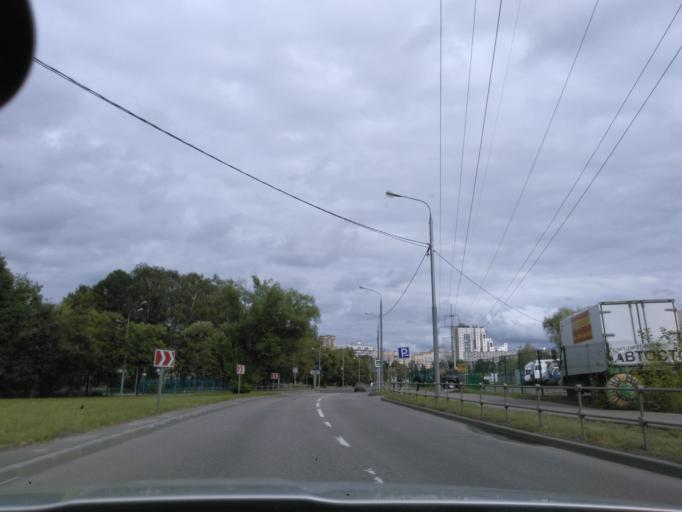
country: RU
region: Moscow
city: Zelenograd
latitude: 56.0094
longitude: 37.1935
